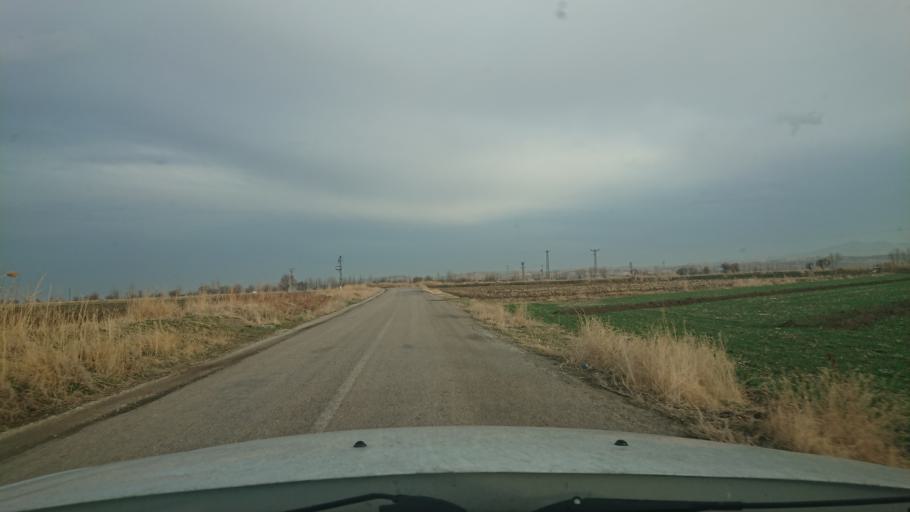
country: TR
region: Aksaray
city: Yesilova
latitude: 38.4373
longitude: 33.8382
